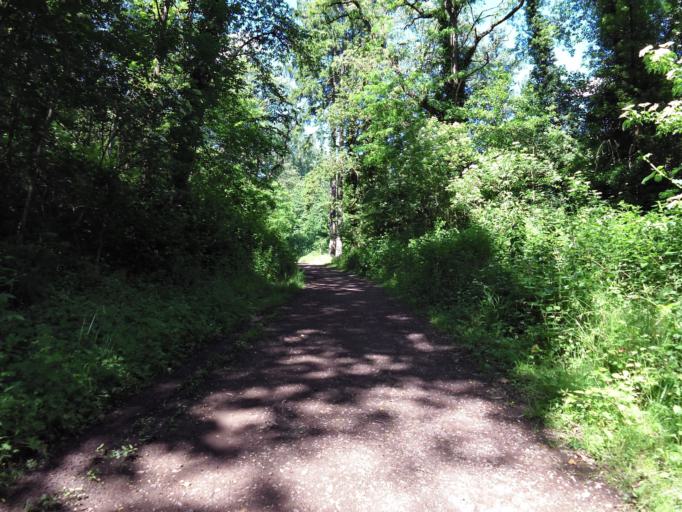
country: DE
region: Rheinland-Pfalz
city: Rhodt unter Rietburg
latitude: 49.2822
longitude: 8.0901
